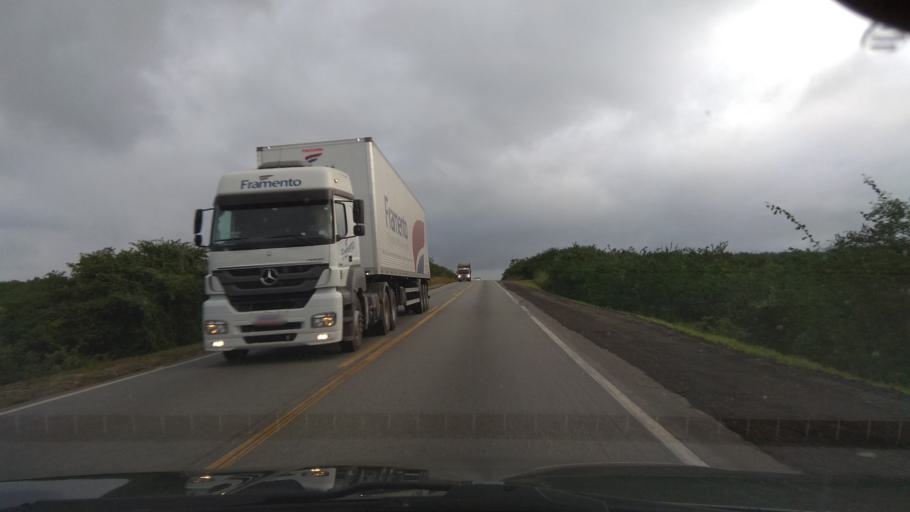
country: BR
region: Bahia
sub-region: Jaguaquara
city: Jaguaquara
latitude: -13.4197
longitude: -40.0268
